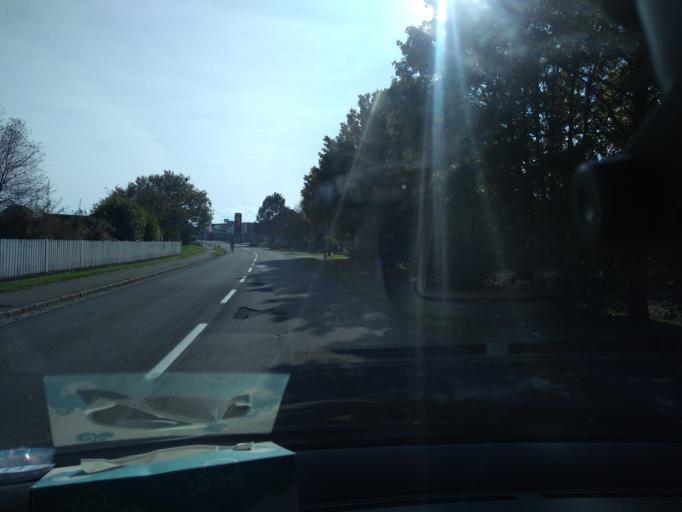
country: AT
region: Styria
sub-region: Politischer Bezirk Leibnitz
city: Lang
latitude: 46.8486
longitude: 15.5379
